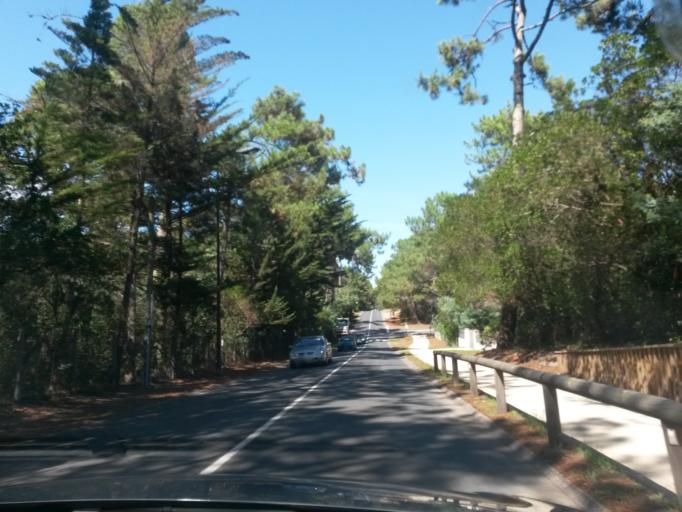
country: FR
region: Aquitaine
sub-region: Departement de la Gironde
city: Arcachon
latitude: 44.6602
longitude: -1.2439
